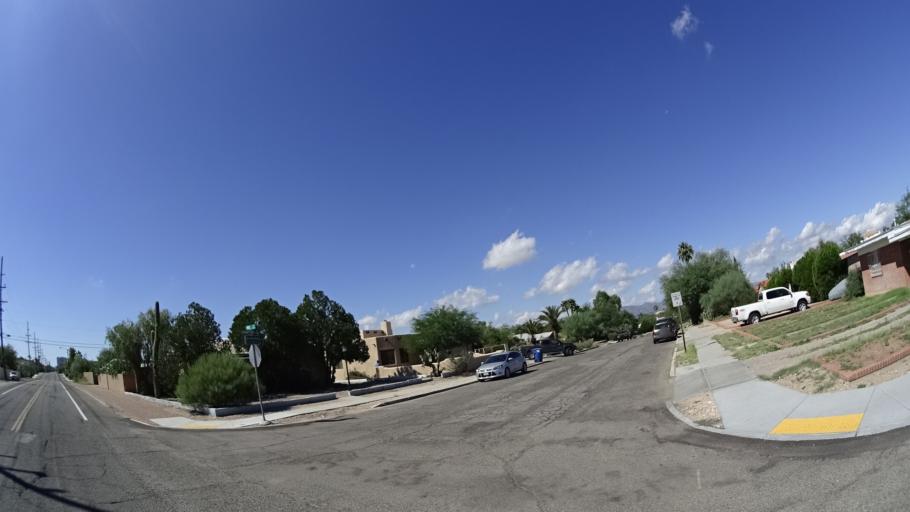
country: US
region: Arizona
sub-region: Pima County
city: Tucson
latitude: 32.2479
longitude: -110.9569
